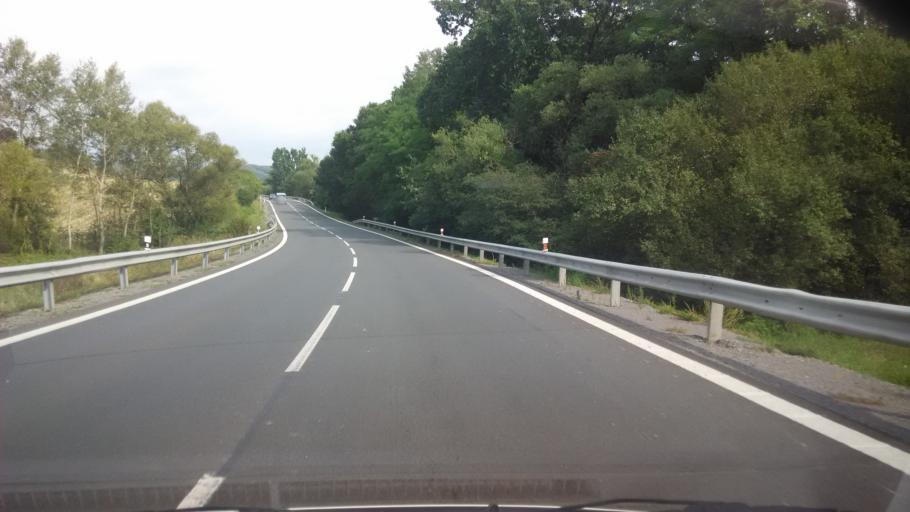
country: SK
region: Banskobystricky
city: Krupina
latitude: 48.3182
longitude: 19.0513
